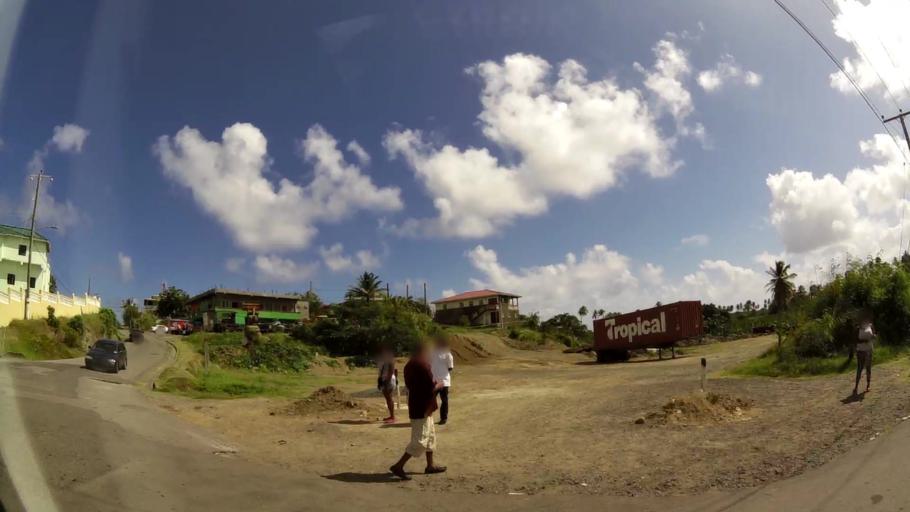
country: LC
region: Micoud Quarter
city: Micoud
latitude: 13.8175
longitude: -60.9010
